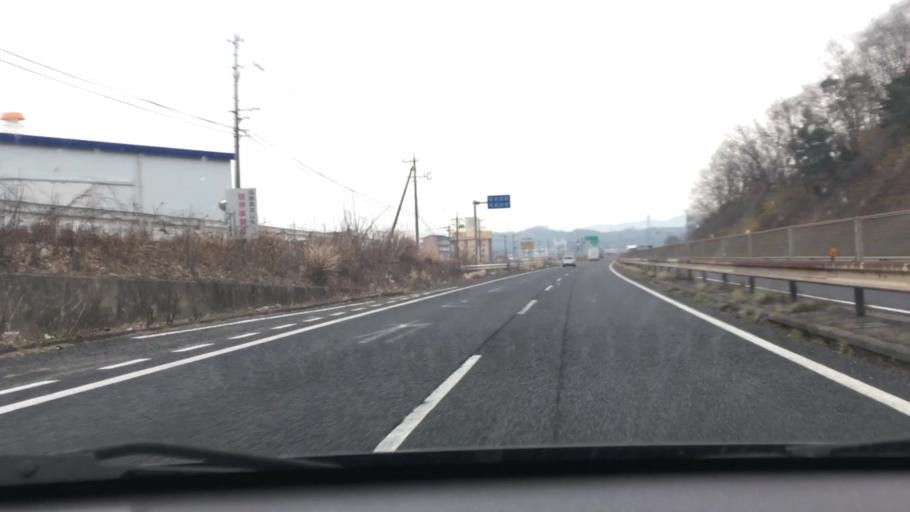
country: JP
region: Mie
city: Ueno-ebisumachi
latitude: 34.7364
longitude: 136.1054
